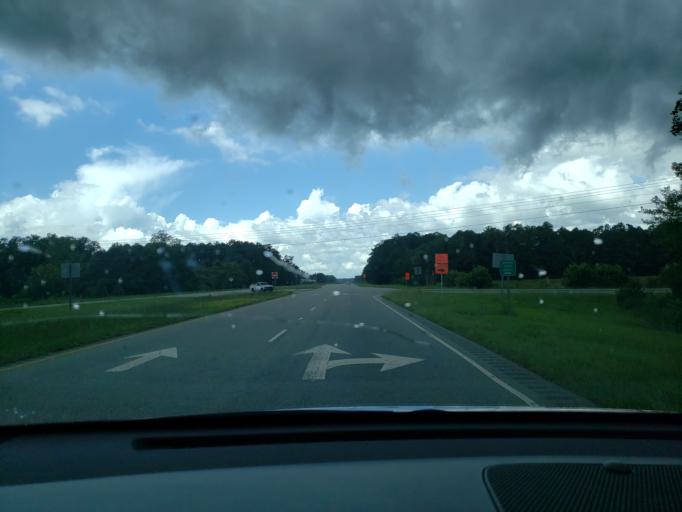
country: US
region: North Carolina
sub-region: Bladen County
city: Elizabethtown
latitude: 34.6146
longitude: -78.6421
